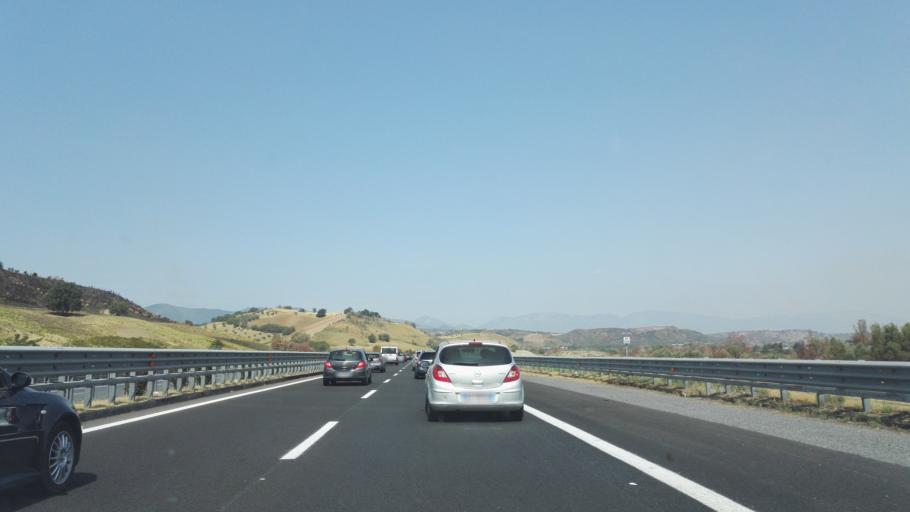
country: IT
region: Calabria
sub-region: Provincia di Cosenza
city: Taverna
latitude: 39.4560
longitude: 16.2318
